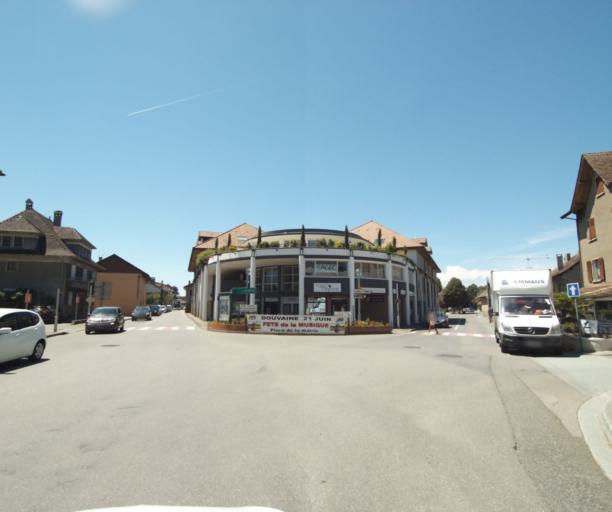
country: FR
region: Rhone-Alpes
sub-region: Departement de la Haute-Savoie
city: Douvaine
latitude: 46.3058
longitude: 6.3013
